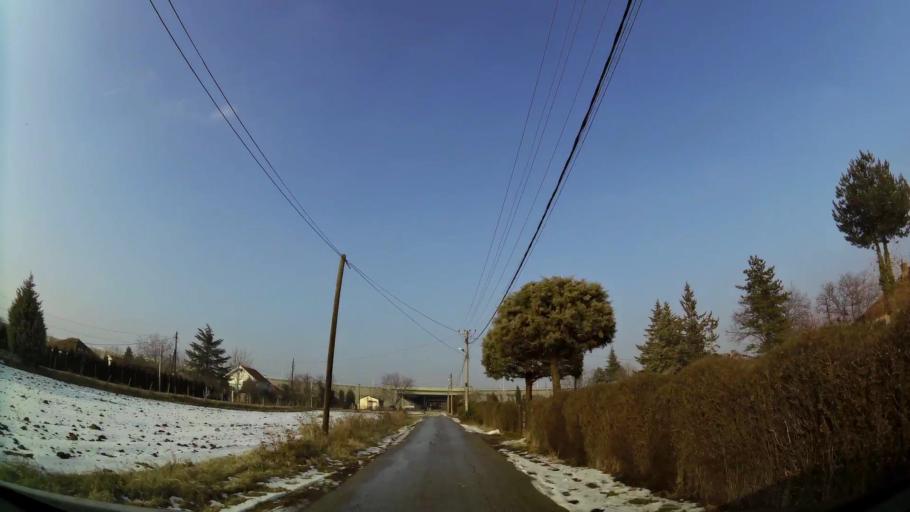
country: MK
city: Miladinovci
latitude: 41.9819
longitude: 21.6503
